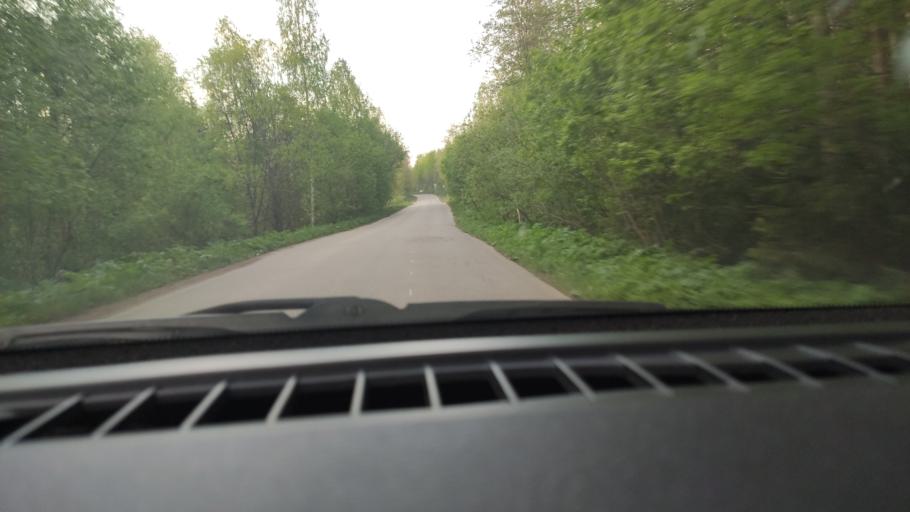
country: RU
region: Perm
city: Overyata
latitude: 58.0752
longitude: 56.0017
